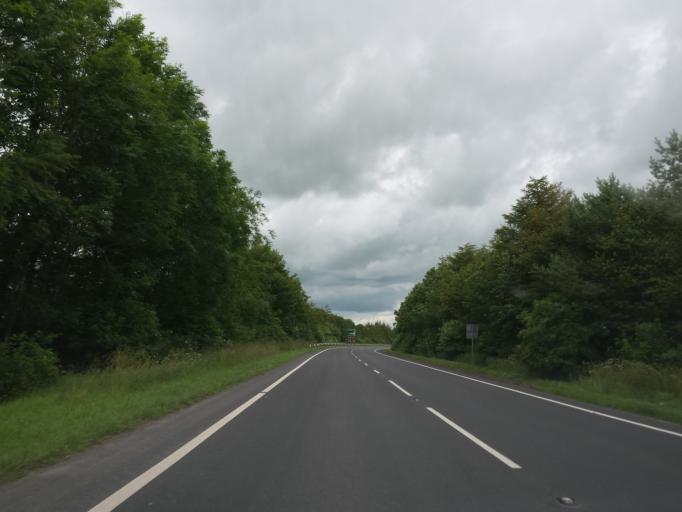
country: GB
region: Scotland
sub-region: Dumfries and Galloway
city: Castle Douglas
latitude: 54.9426
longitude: -3.9456
